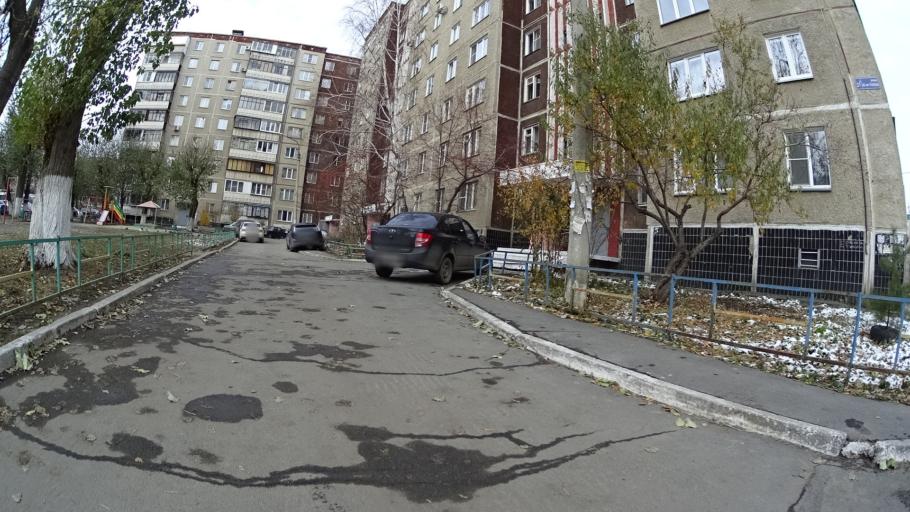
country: RU
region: Chelyabinsk
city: Roshchino
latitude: 55.1878
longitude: 61.2990
